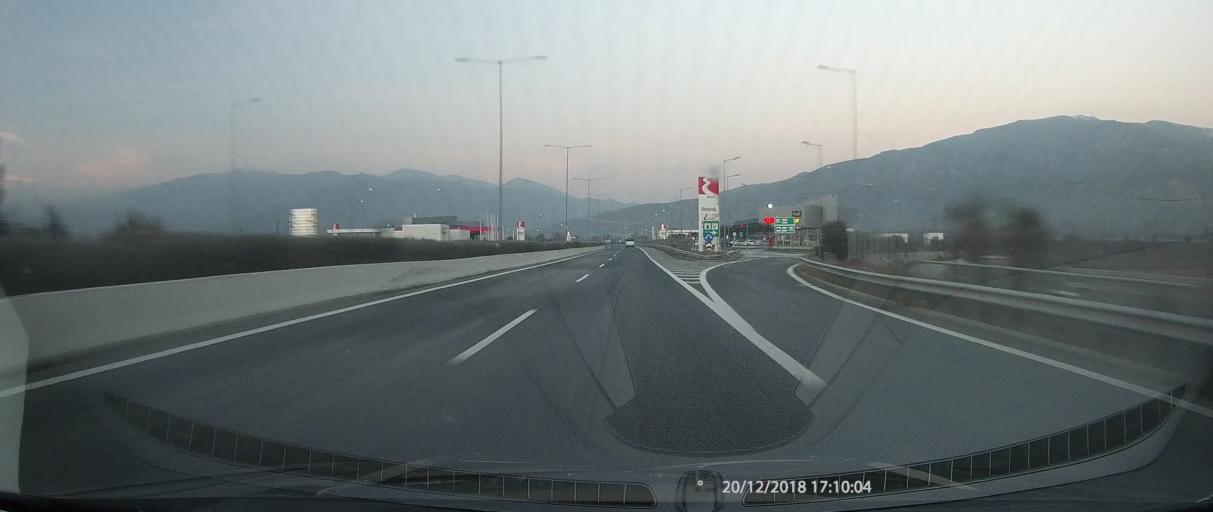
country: GR
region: Thessaly
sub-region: Nomos Larisis
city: Makrychori
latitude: 39.8125
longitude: 22.5070
